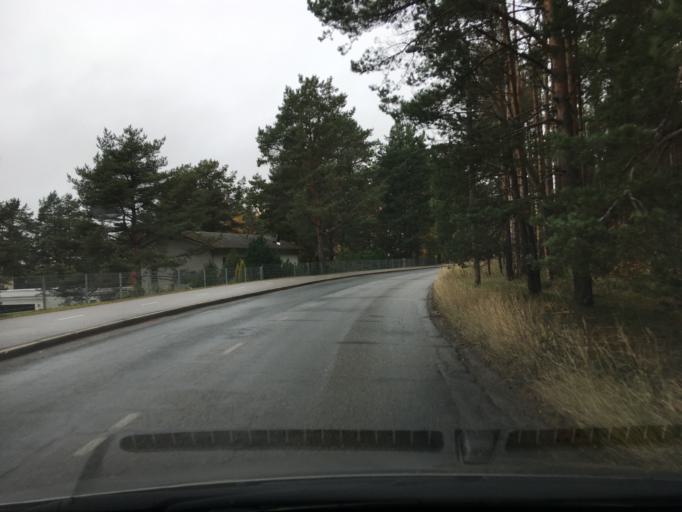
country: EE
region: Tartu
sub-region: Tartu linn
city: Tartu
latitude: 58.3490
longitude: 26.7690
